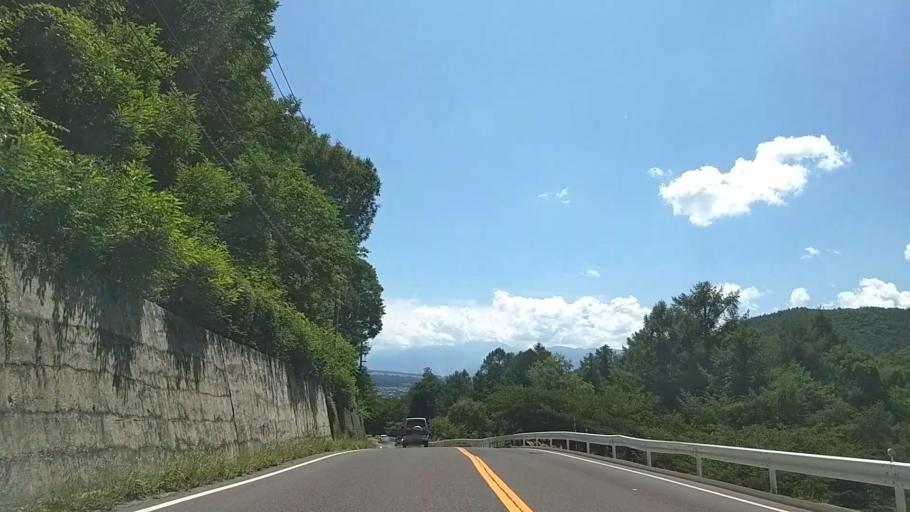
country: JP
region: Nagano
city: Chino
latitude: 36.0744
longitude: 138.2229
